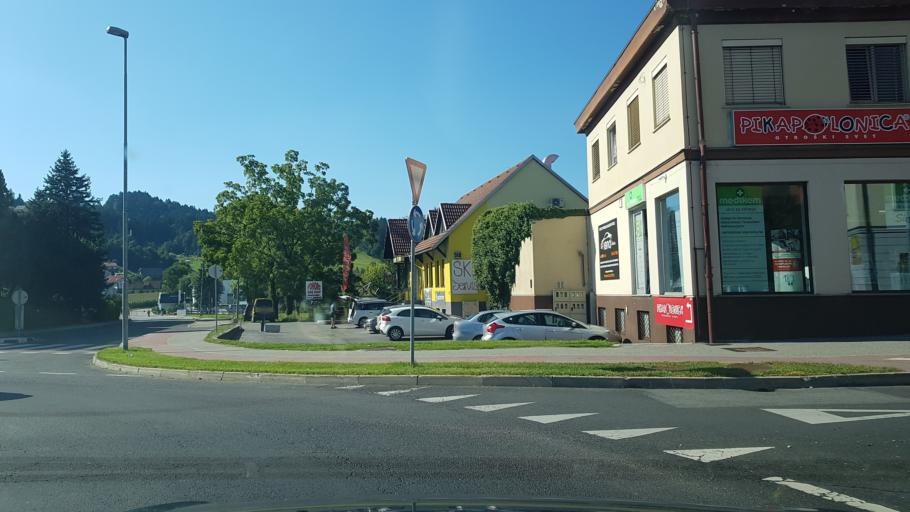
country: SI
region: Slovenj Gradec
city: Slovenj Gradec
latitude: 46.5078
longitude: 15.0772
